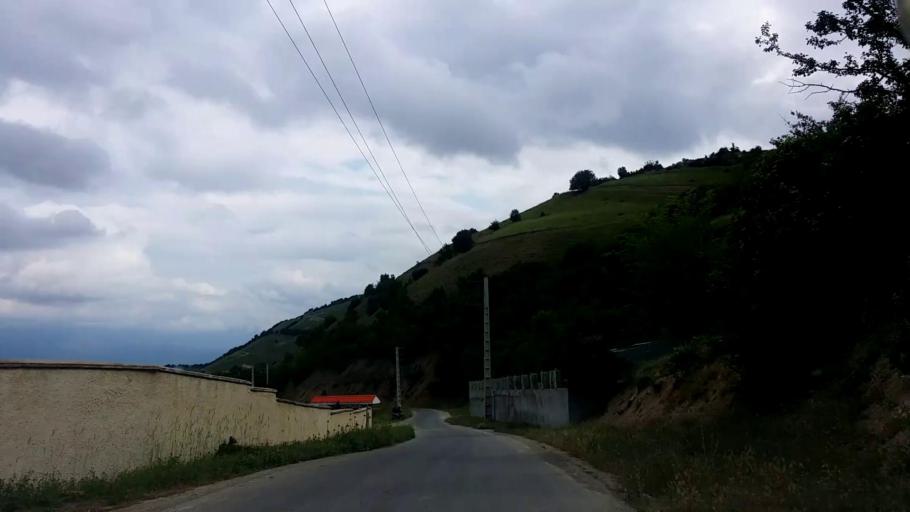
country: IR
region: Mazandaran
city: Chalus
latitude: 36.5510
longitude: 51.2701
